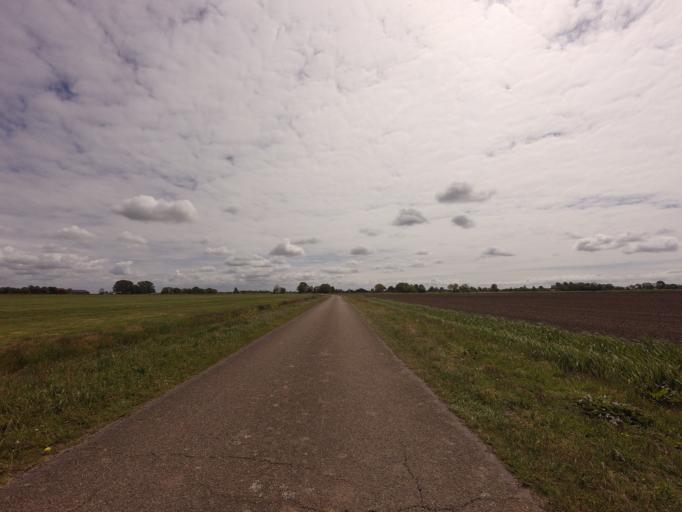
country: NL
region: Friesland
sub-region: Gemeente Gaasterlan-Sleat
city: Balk
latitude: 52.9171
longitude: 5.5296
